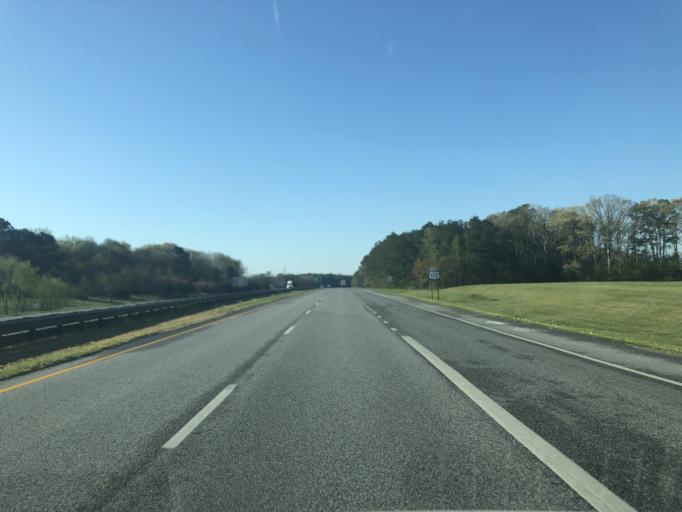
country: US
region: Maryland
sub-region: Worcester County
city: Snow Hill
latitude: 38.1724
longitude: -75.3732
